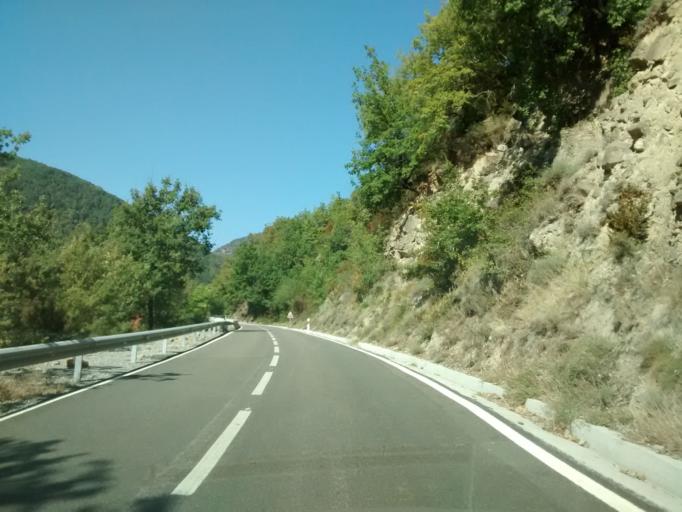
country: ES
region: Aragon
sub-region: Provincia de Huesca
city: Fiscal
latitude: 42.5293
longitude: -0.1340
